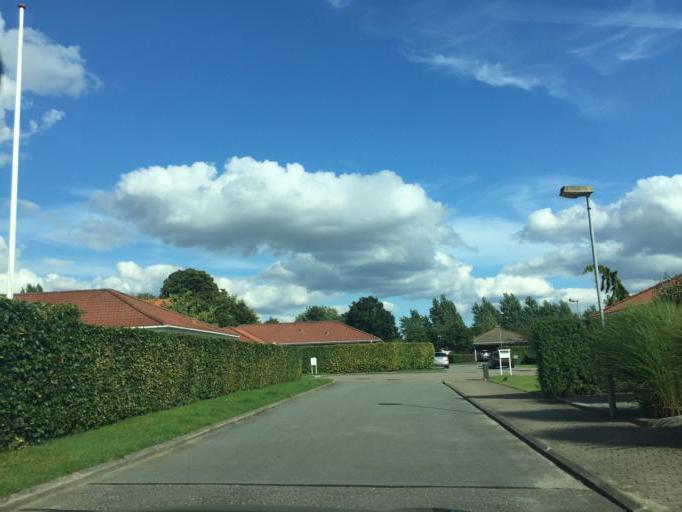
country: DK
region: South Denmark
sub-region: Odense Kommune
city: Odense
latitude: 55.3670
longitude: 10.4043
